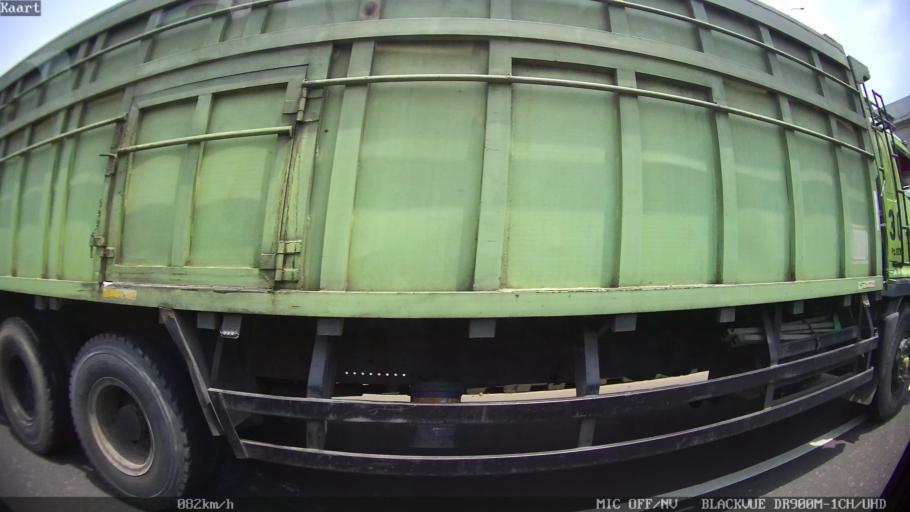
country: ID
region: Banten
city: Serang
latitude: -6.1388
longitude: 106.2484
